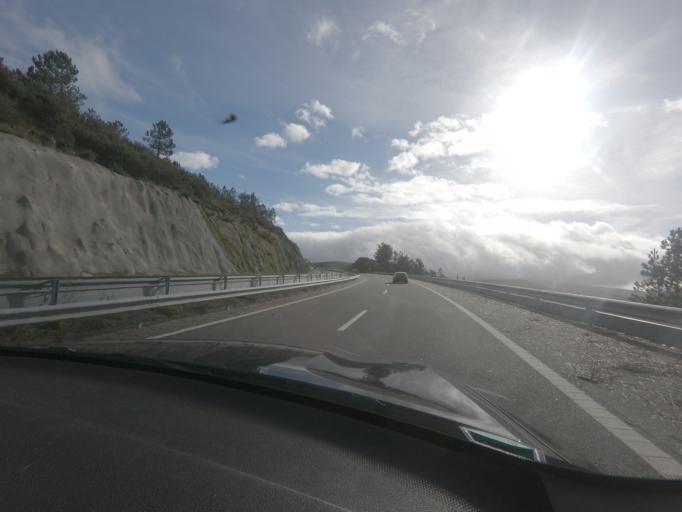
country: PT
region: Viseu
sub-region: Lamego
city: Lamego
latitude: 41.0446
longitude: -7.8602
